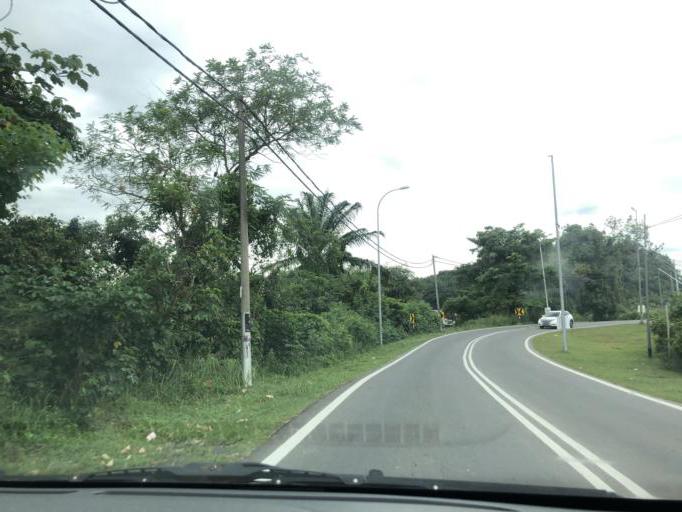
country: MY
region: Putrajaya
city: Putrajaya
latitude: 2.9183
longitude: 101.7512
